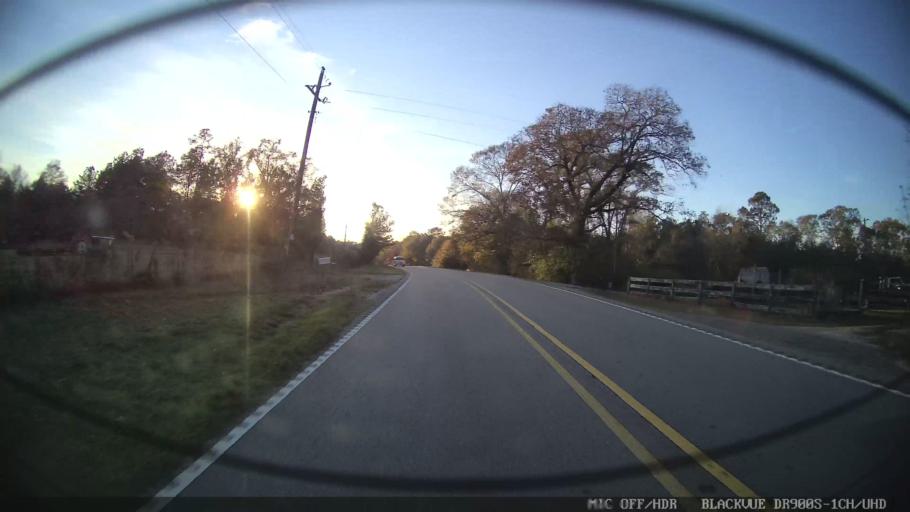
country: US
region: Mississippi
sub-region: Lamar County
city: Lumberton
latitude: 30.9954
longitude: -89.3739
